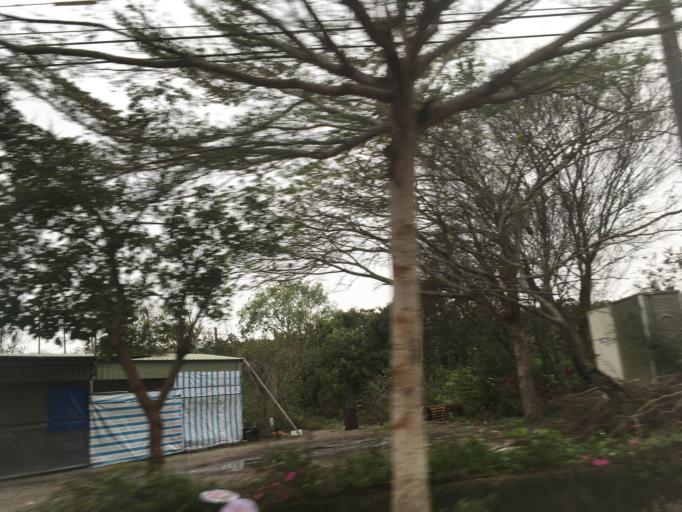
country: TW
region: Taiwan
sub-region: Miaoli
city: Miaoli
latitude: 24.4289
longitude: 120.7273
